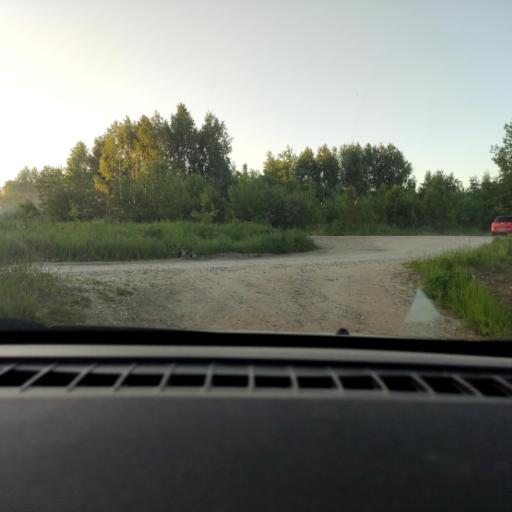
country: RU
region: Perm
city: Polazna
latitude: 58.1751
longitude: 56.4009
